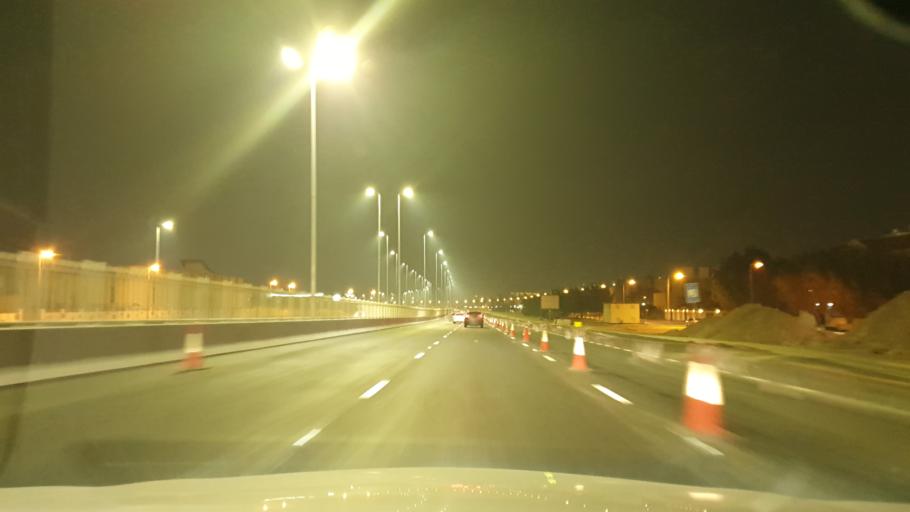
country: BH
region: Northern
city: Madinat `Isa
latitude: 26.1573
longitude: 50.5489
